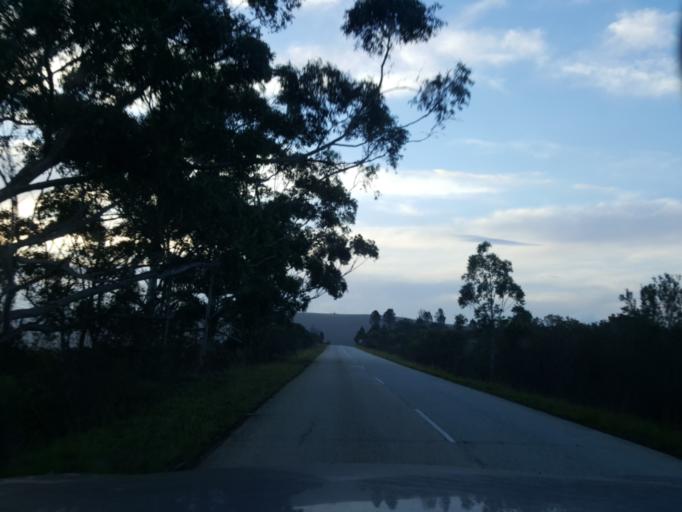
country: ZA
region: Eastern Cape
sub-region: Cacadu District Municipality
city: Grahamstown
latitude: -33.3852
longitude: 26.4716
